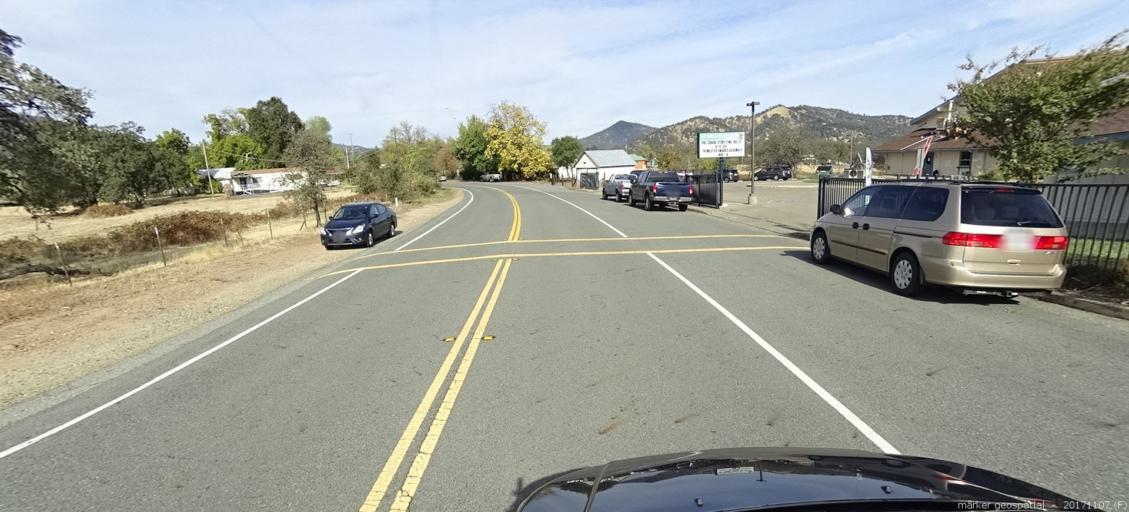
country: US
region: California
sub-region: Shasta County
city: Shasta
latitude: 40.5031
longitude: -122.5413
